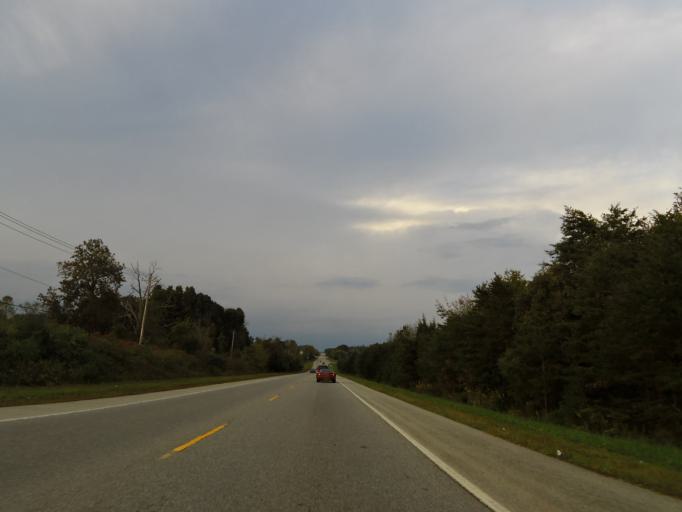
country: US
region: Tennessee
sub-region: Monroe County
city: Vonore
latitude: 35.6014
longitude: -84.2735
